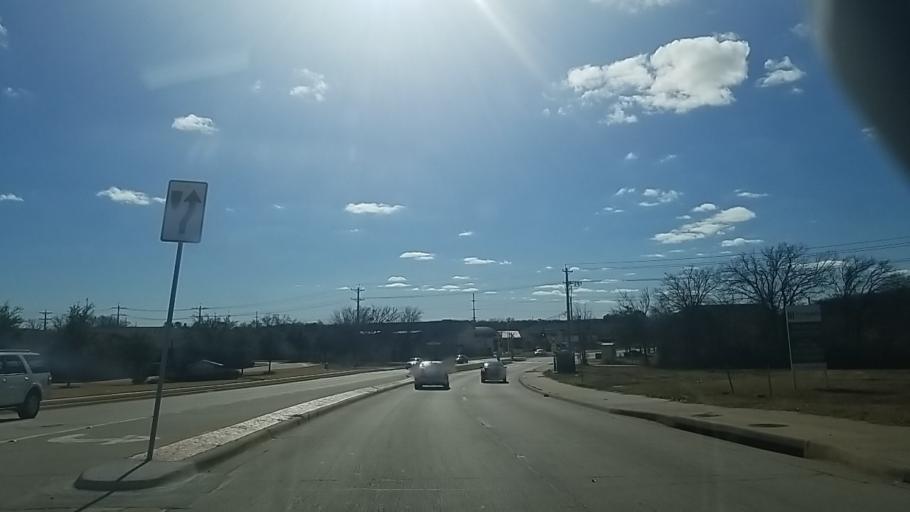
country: US
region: Texas
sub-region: Denton County
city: Corinth
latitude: 33.1865
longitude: -97.0959
